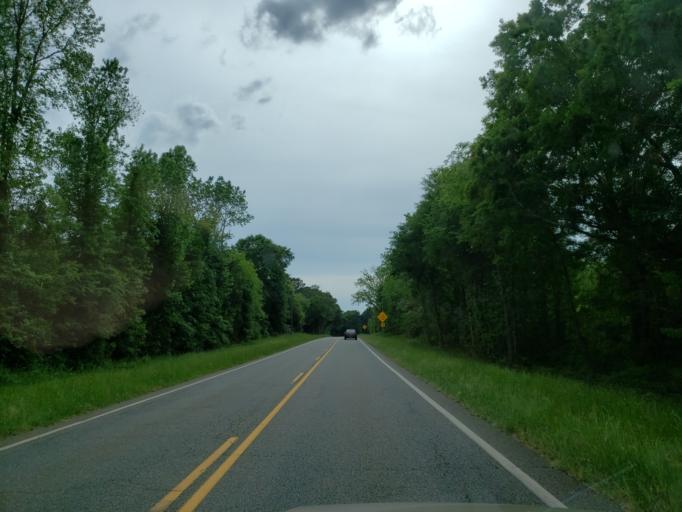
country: US
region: Georgia
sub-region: Macon County
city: Marshallville
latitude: 32.4157
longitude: -83.8584
